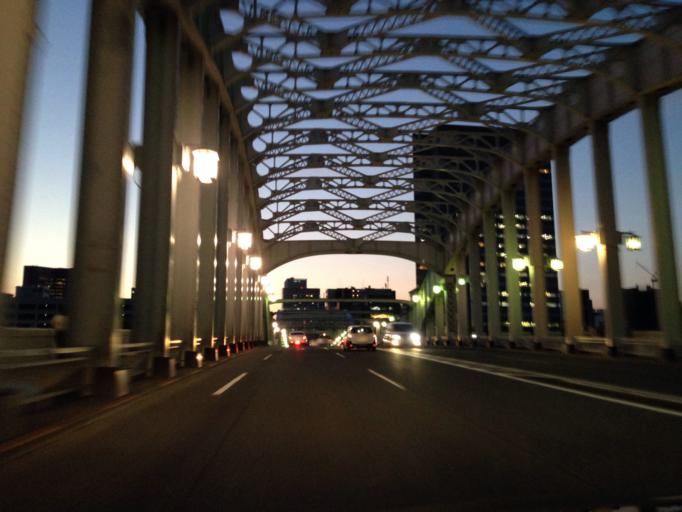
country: JP
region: Tokyo
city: Tokyo
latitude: 35.6614
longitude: 139.7756
